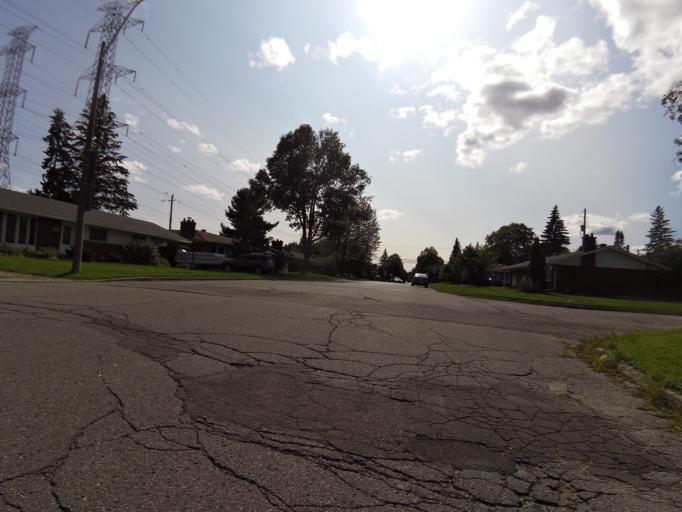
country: CA
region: Ontario
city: Ottawa
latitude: 45.3609
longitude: -75.6737
